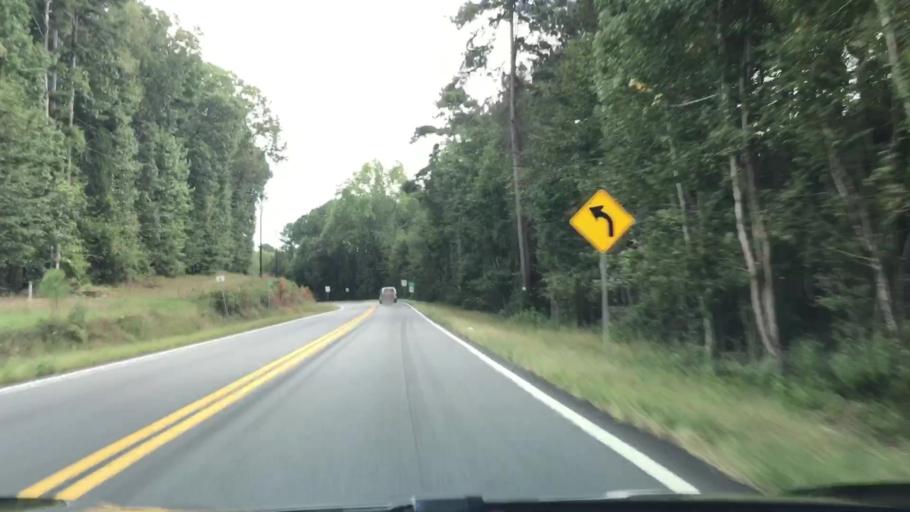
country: US
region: Georgia
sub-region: Greene County
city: Union Point
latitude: 33.5410
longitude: -83.0926
